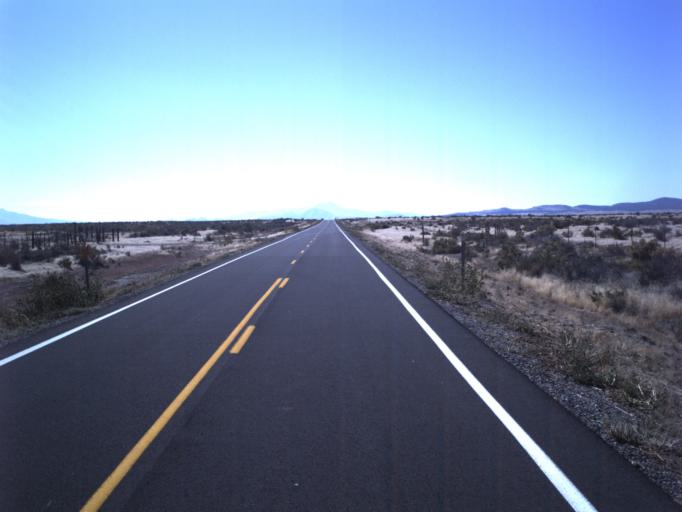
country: US
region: Utah
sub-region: Tooele County
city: Grantsville
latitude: 40.3446
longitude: -112.7451
